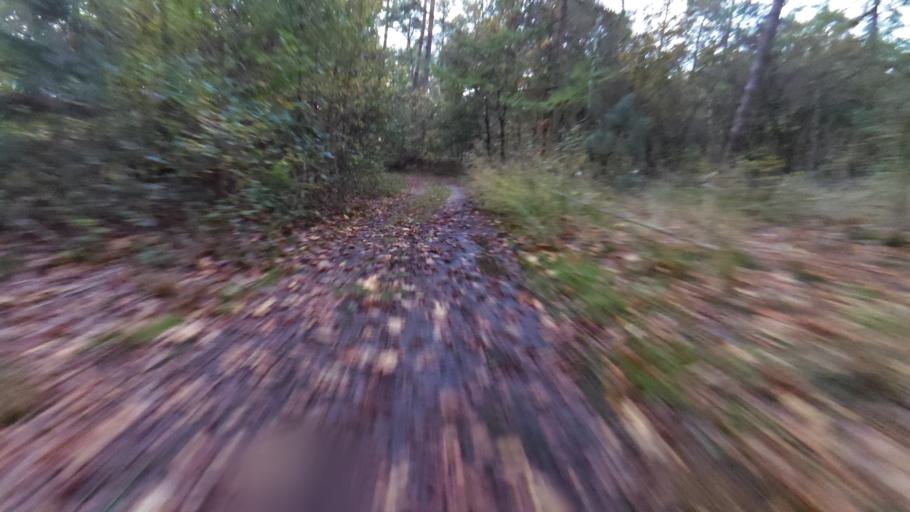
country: NL
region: Gelderland
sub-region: Gemeente Renkum
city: Oosterbeek
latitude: 52.0190
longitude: 5.8362
